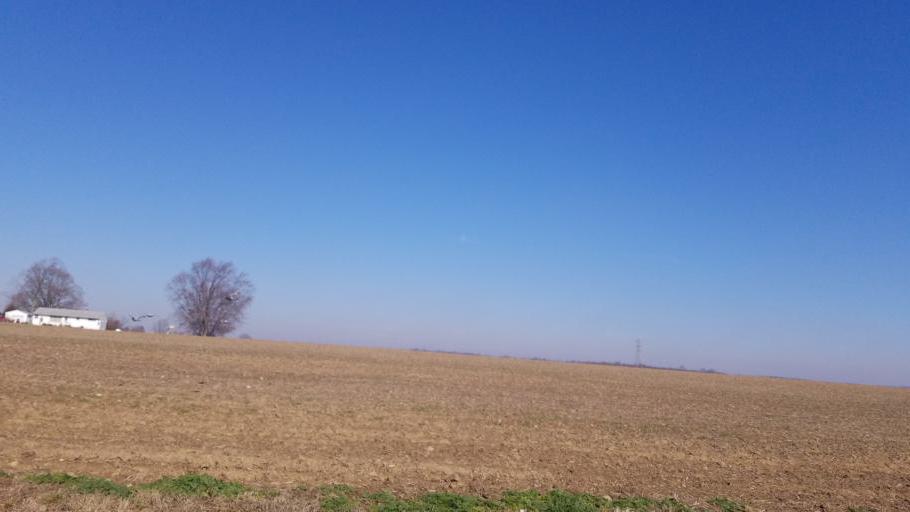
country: US
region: Ohio
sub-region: Richland County
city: Lincoln Heights
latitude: 40.8485
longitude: -82.5124
